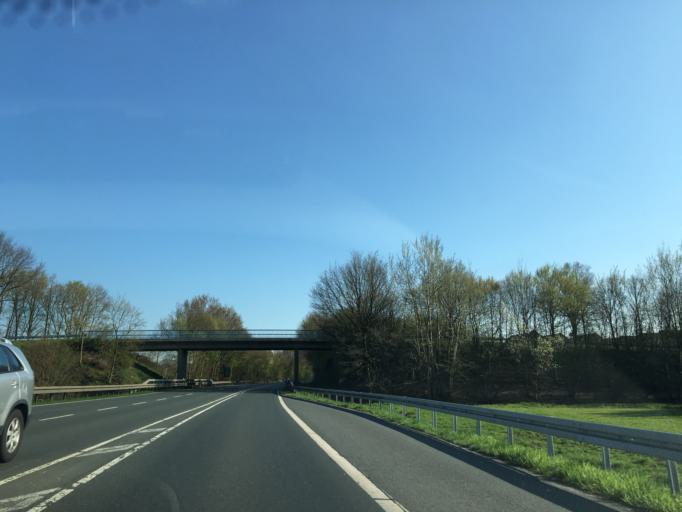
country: DE
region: North Rhine-Westphalia
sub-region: Regierungsbezirk Munster
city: Greven
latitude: 52.1047
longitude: 7.6276
